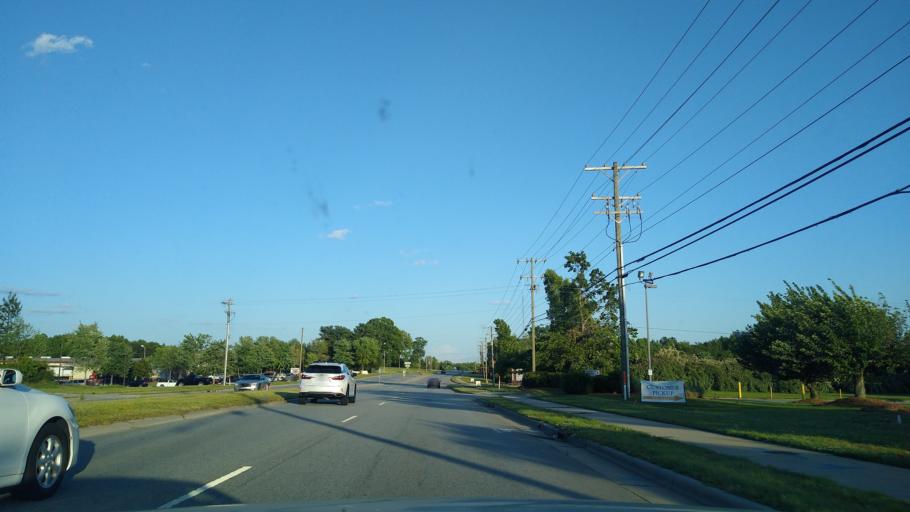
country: US
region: North Carolina
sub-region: Guilford County
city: Oak Ridge
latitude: 36.1018
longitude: -79.9807
